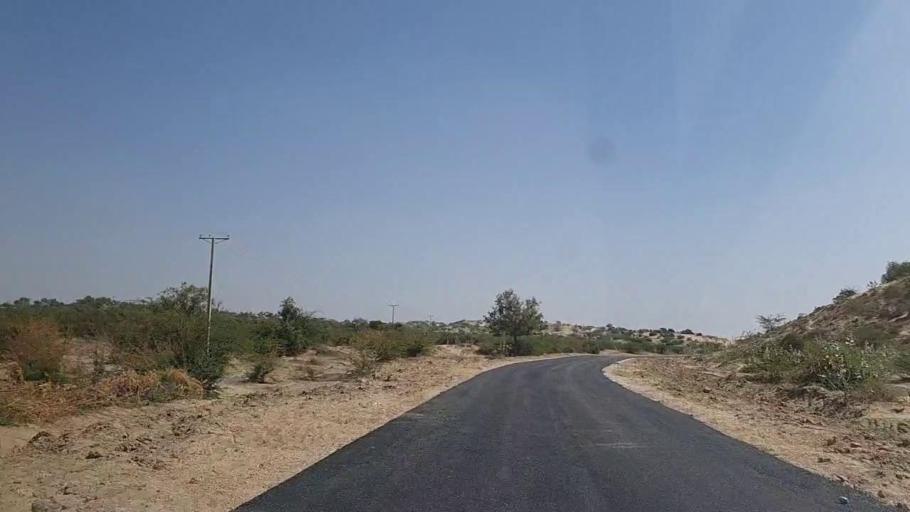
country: PK
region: Sindh
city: Diplo
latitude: 24.4812
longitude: 69.5234
